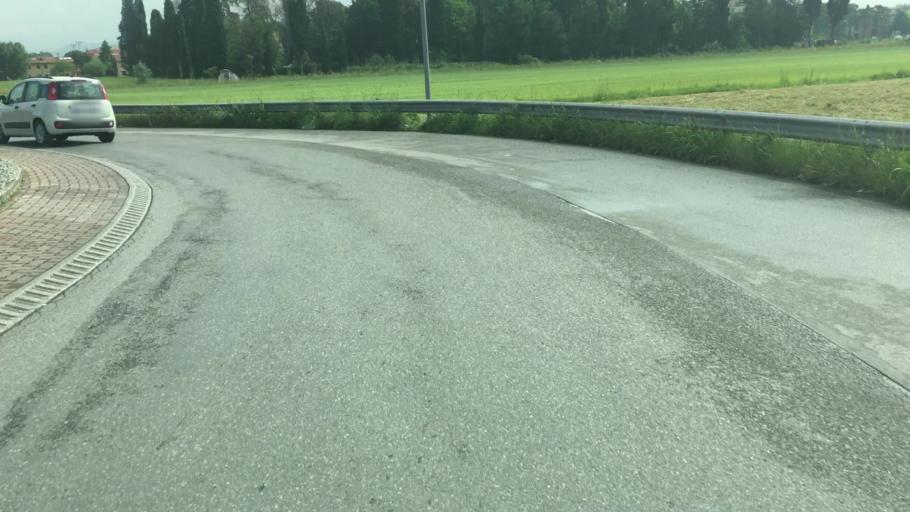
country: IT
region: Tuscany
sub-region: Province of Florence
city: Campi Bisenzio
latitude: 43.8205
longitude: 11.1232
